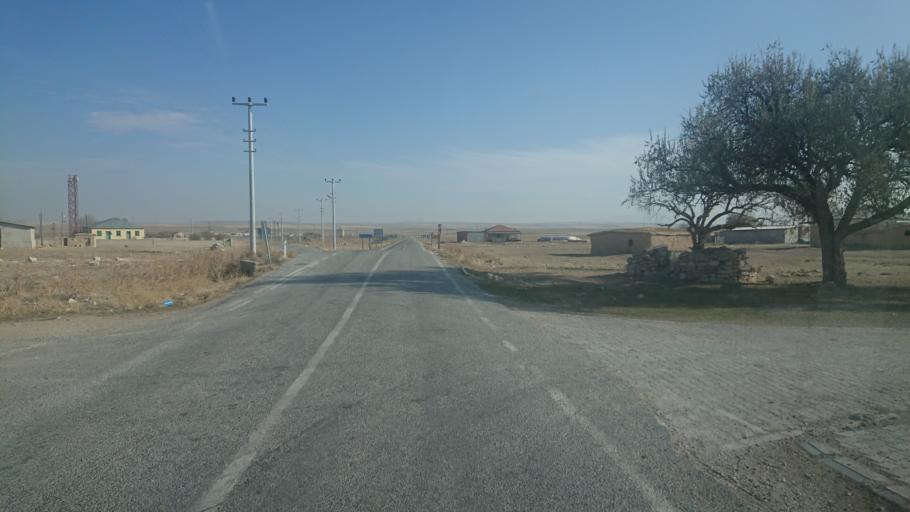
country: TR
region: Aksaray
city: Sultanhani
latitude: 38.0396
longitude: 33.5952
